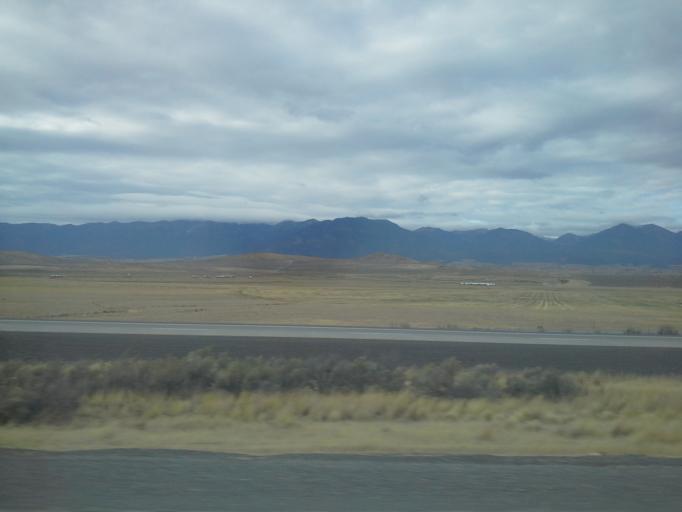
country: US
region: Oregon
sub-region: Baker County
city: Baker City
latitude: 44.9440
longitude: -117.8459
